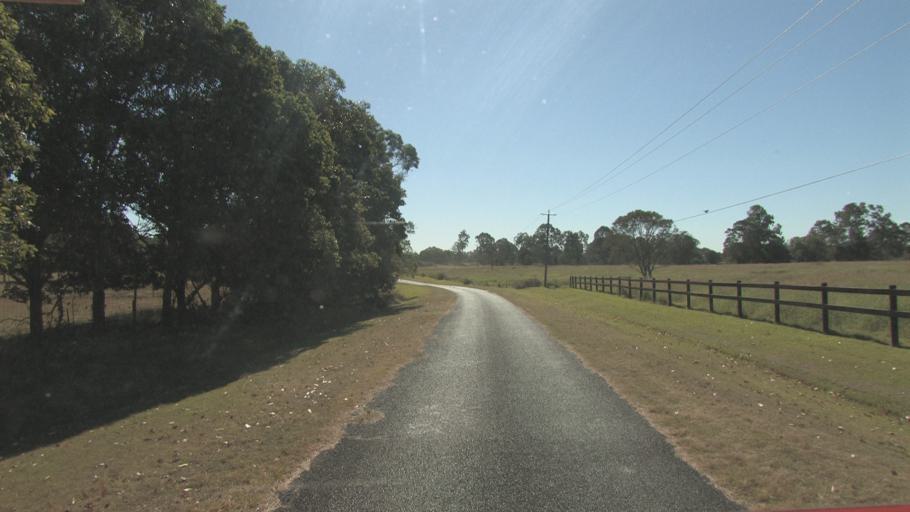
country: AU
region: Queensland
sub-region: Logan
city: Waterford West
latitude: -27.7030
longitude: 153.1295
